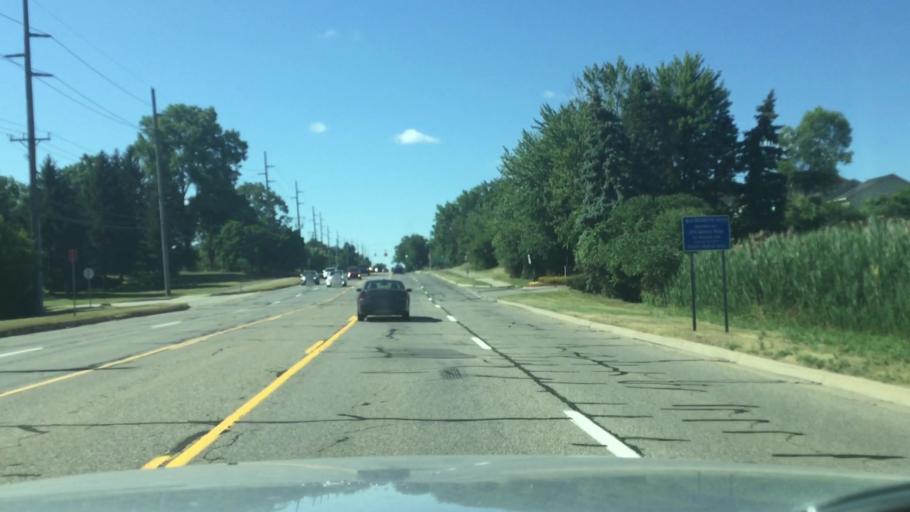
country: US
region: Michigan
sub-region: Oakland County
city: Orchard Lake
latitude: 42.5603
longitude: -83.3616
